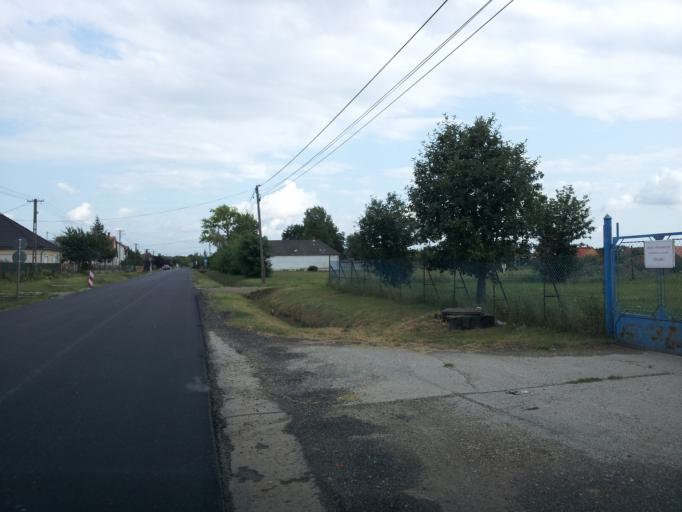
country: HU
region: Fejer
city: Enying
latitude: 46.8922
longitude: 18.2702
